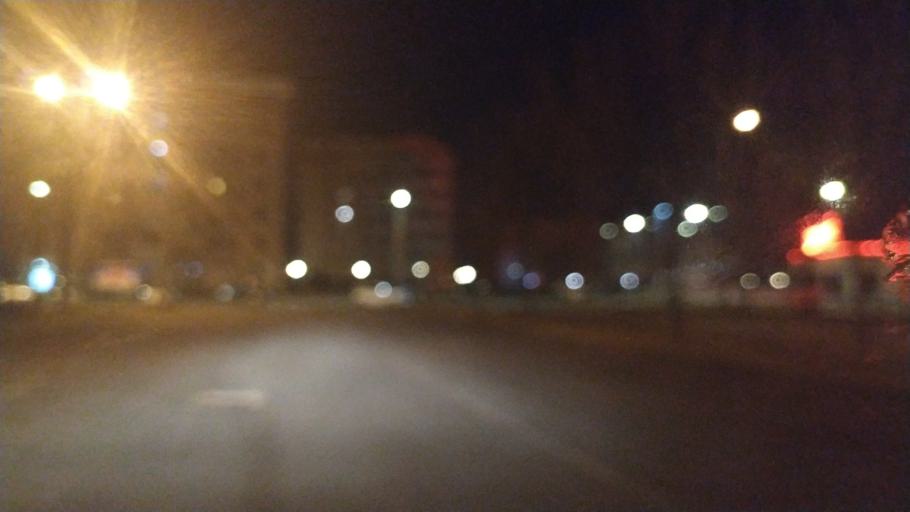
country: IT
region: Piedmont
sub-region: Provincia di Biella
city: Ponderano
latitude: 45.5507
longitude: 8.0633
